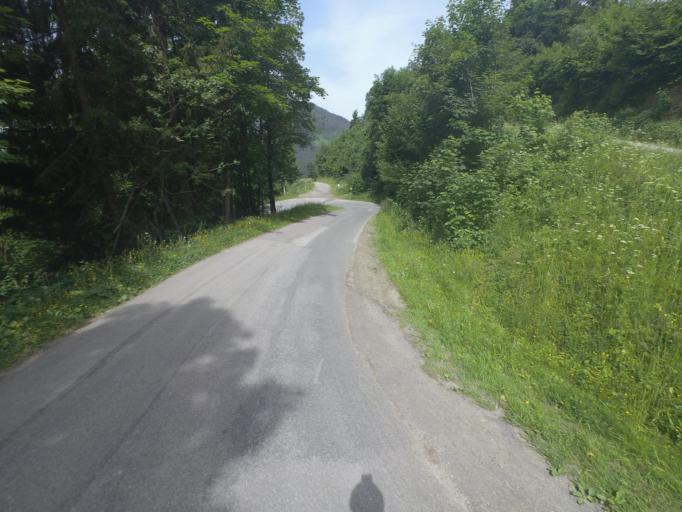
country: AT
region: Salzburg
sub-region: Politischer Bezirk Sankt Johann im Pongau
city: Muhlbach am Hochkonig
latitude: 47.3457
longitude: 13.1241
